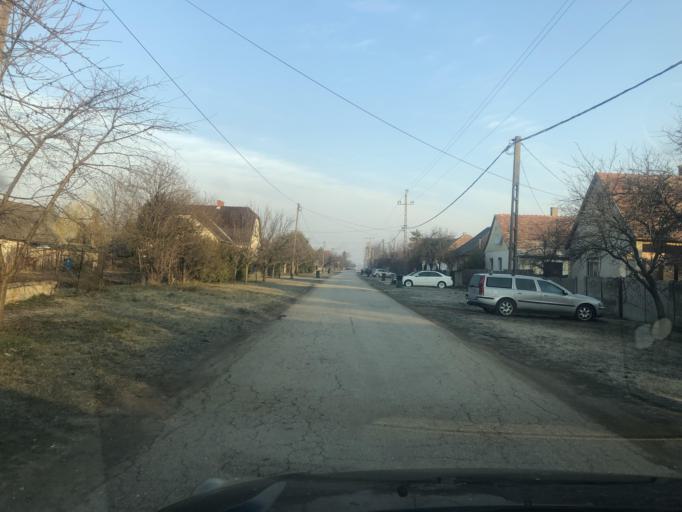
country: HU
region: Fejer
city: Lovasbereny
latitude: 47.3176
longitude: 18.5469
